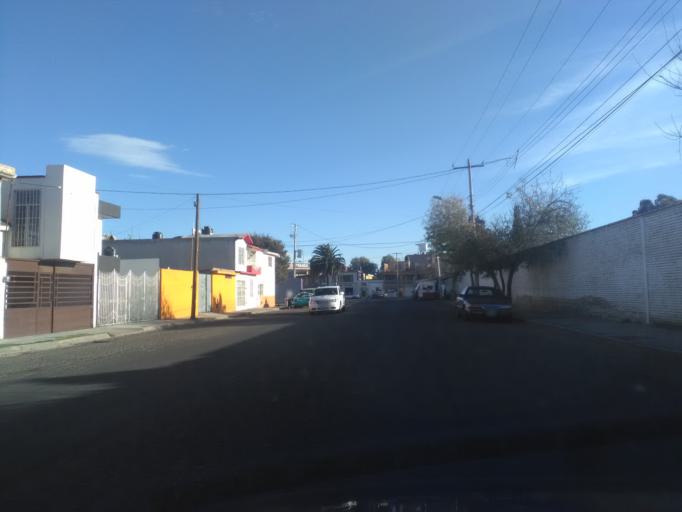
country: MX
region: Durango
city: Victoria de Durango
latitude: 24.0277
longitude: -104.6341
